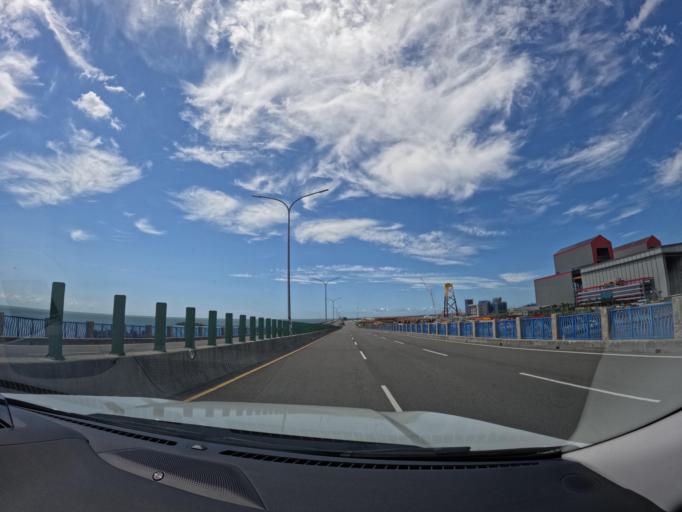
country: TW
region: Taiwan
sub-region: Taoyuan
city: Taoyuan
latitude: 25.1383
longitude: 121.3673
